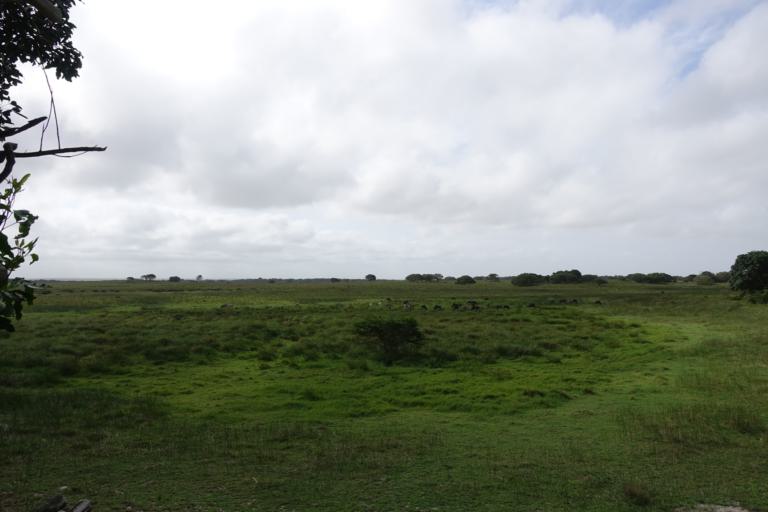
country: ZA
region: KwaZulu-Natal
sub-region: uMkhanyakude District Municipality
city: Hluhluwe
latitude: -28.2596
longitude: 32.4740
